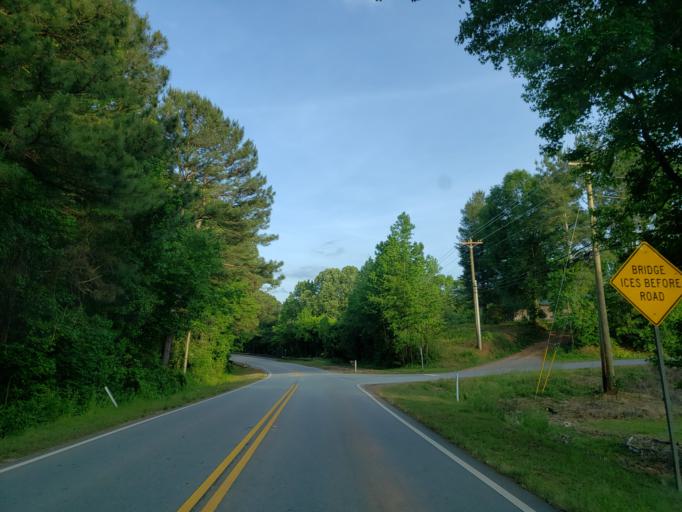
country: US
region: Georgia
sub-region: Carroll County
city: Carrollton
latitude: 33.5935
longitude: -85.1312
